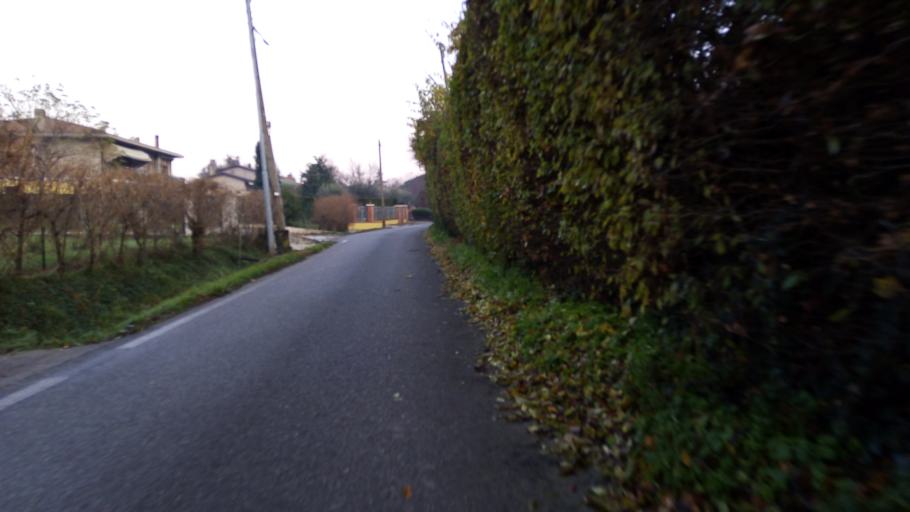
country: IT
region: Veneto
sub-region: Provincia di Padova
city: San Biagio
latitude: 45.3559
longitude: 11.7578
